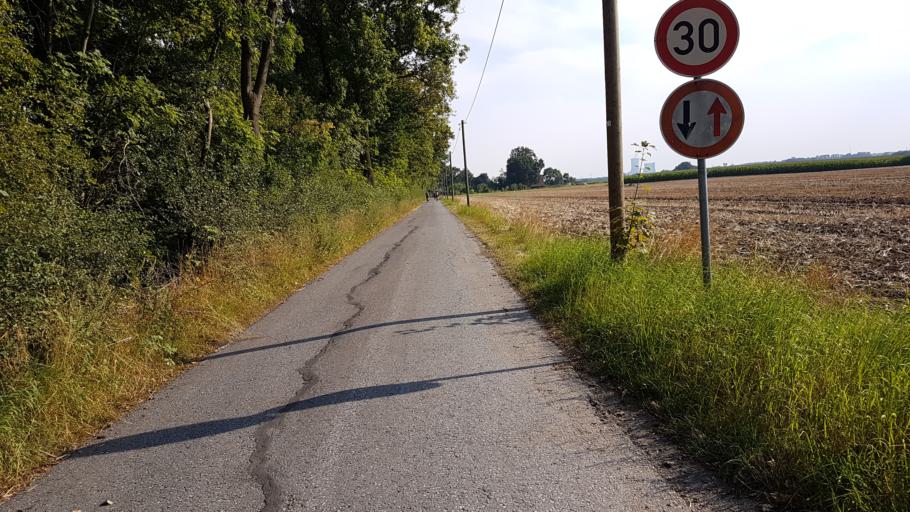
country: DE
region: North Rhine-Westphalia
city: Olfen
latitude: 51.6899
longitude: 7.3770
